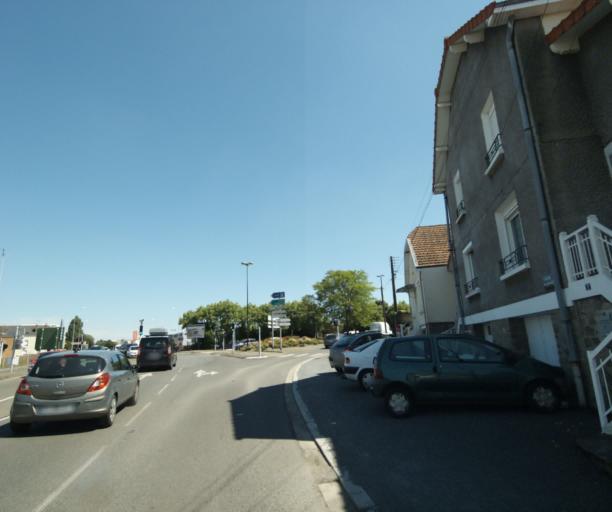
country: FR
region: Pays de la Loire
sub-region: Departement de la Mayenne
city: Laval
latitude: 48.0753
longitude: -0.7531
